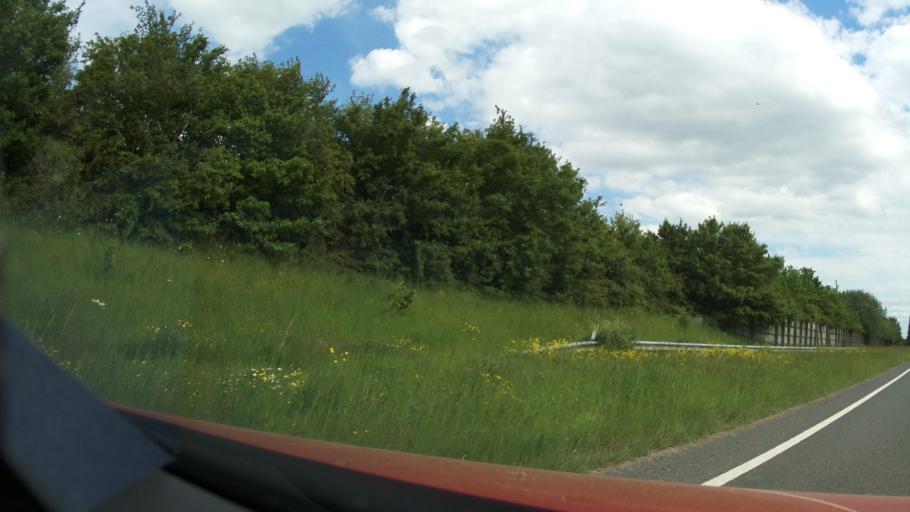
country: GB
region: England
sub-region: Worcestershire
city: Bransford
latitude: 52.1863
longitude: -2.2641
